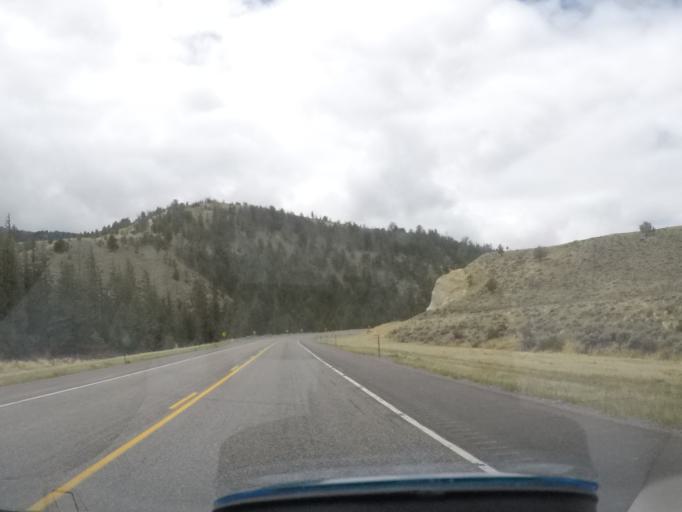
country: US
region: Wyoming
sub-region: Sublette County
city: Pinedale
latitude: 43.5789
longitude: -109.7573
